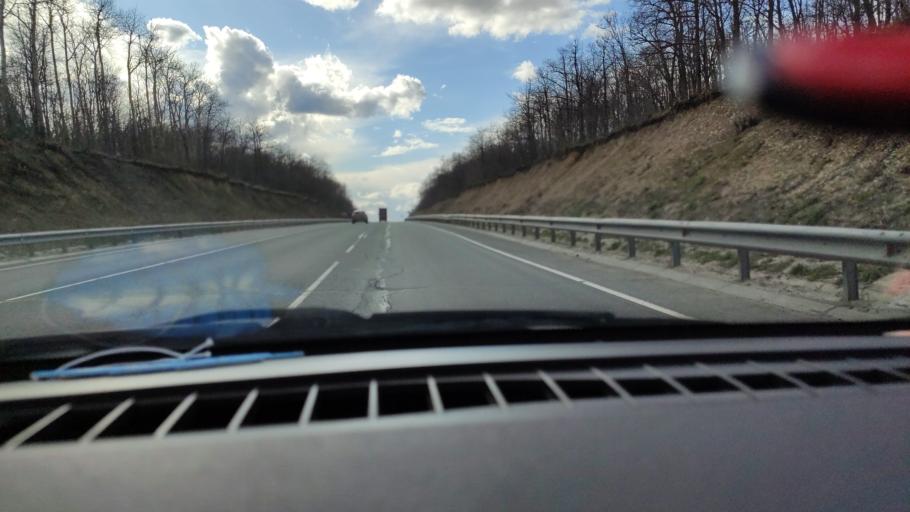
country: RU
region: Saratov
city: Vol'sk
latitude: 52.1079
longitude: 47.3990
